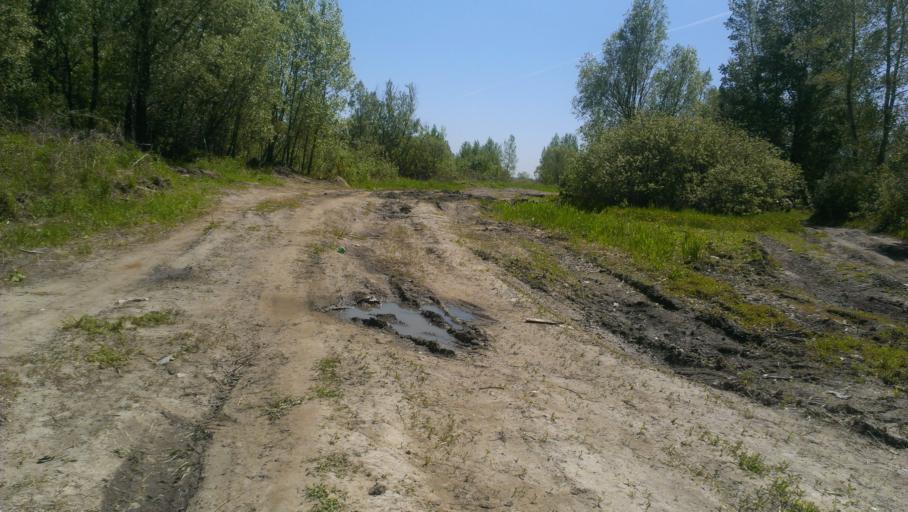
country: RU
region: Altai Krai
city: Zaton
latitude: 53.3139
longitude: 83.8516
